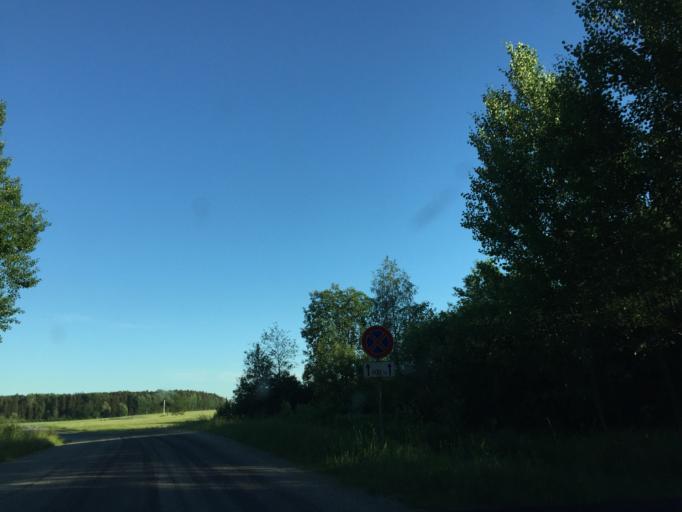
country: LV
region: Broceni
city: Broceni
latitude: 56.7112
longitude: 22.5030
